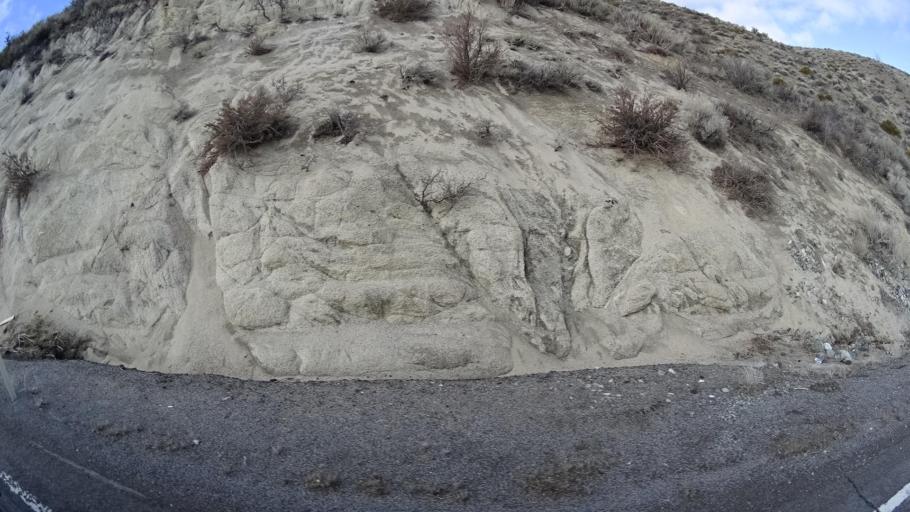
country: US
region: Nevada
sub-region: Washoe County
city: Cold Springs
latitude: 39.8226
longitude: -119.9373
